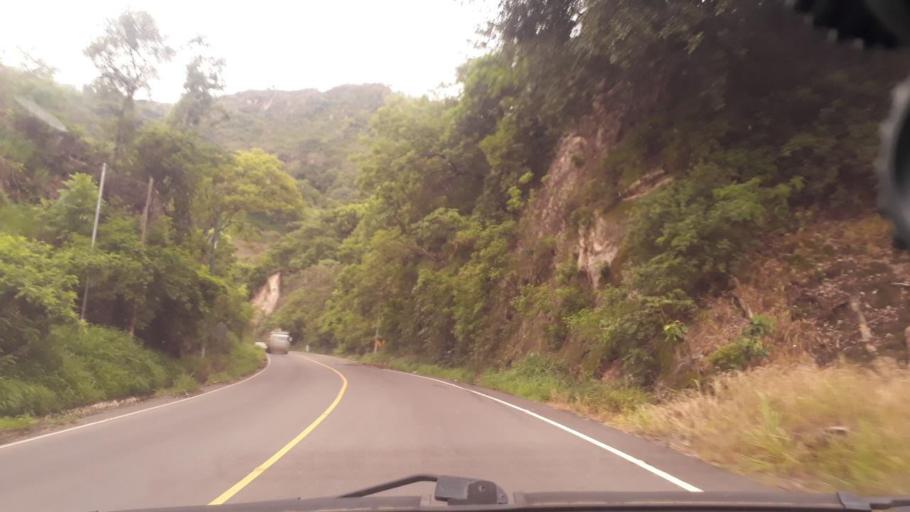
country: GT
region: Chiquimula
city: Quezaltepeque
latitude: 14.6240
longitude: -89.4718
